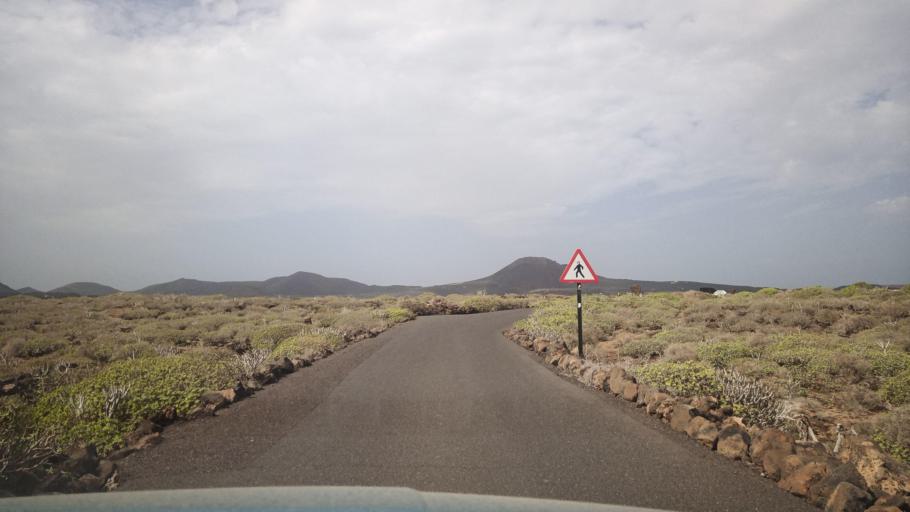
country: ES
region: Canary Islands
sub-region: Provincia de Las Palmas
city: Haria
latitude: 29.1599
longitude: -13.4380
